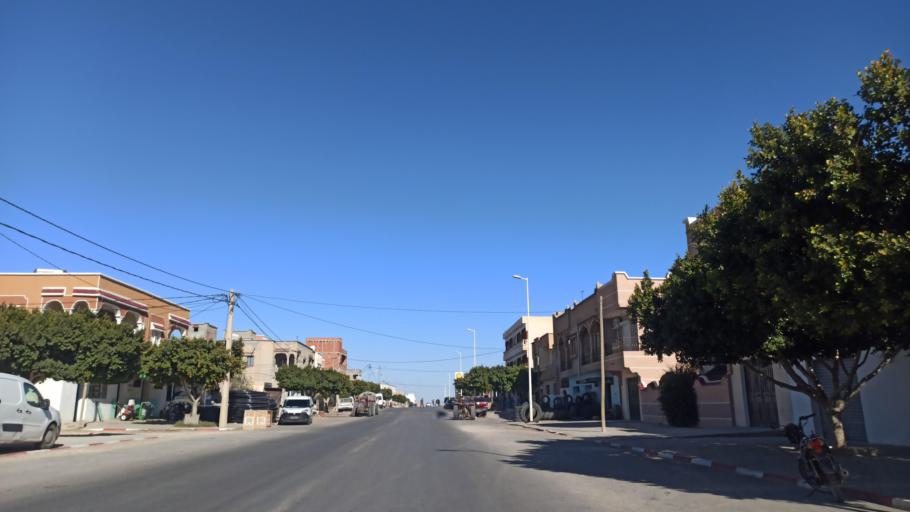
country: TN
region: Sidi Bu Zayd
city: Bi'r al Hufayy
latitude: 34.9377
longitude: 9.2005
